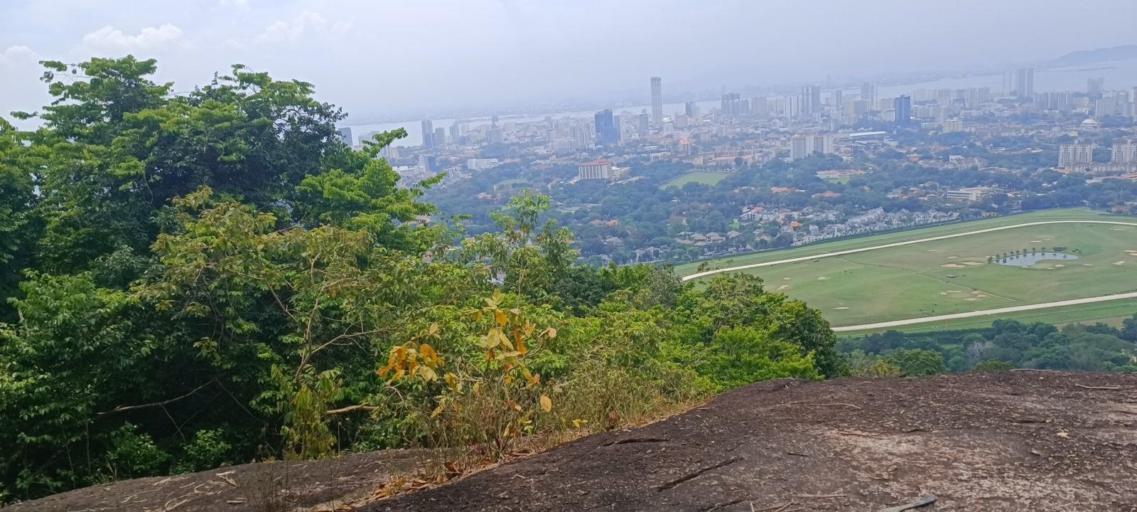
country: MY
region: Penang
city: Tanjung Tokong
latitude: 5.4218
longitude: 100.2921
